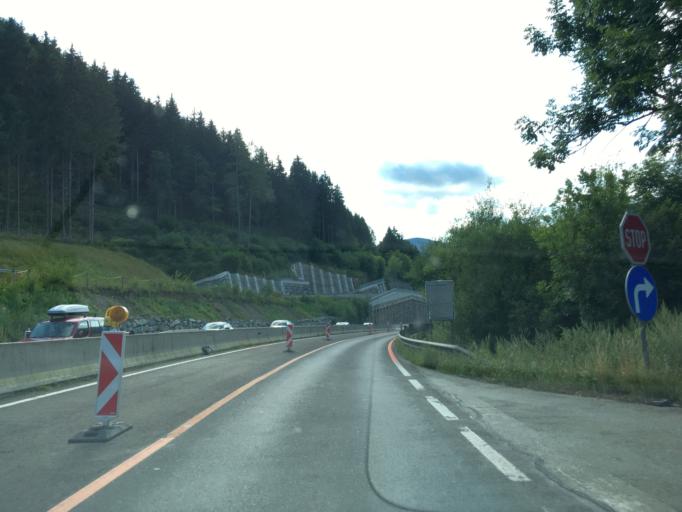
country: AT
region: Styria
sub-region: Politischer Bezirk Murtal
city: Sankt Georgen ob Judenburg
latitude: 47.2076
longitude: 14.4868
